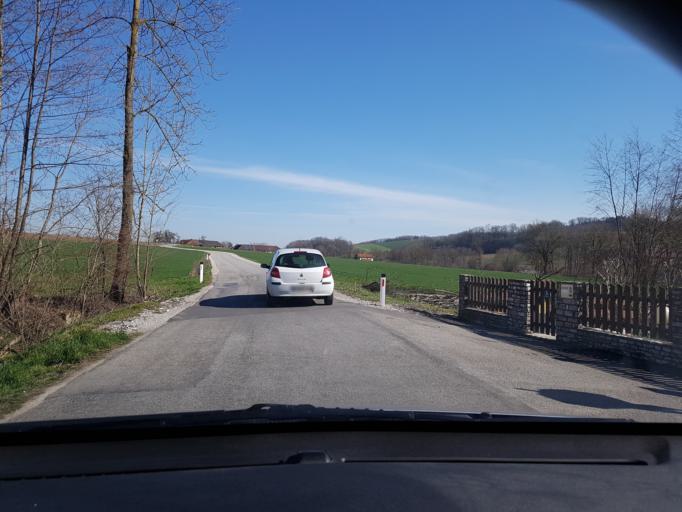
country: AT
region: Upper Austria
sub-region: Politischer Bezirk Linz-Land
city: Ansfelden
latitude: 48.1996
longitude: 14.3121
